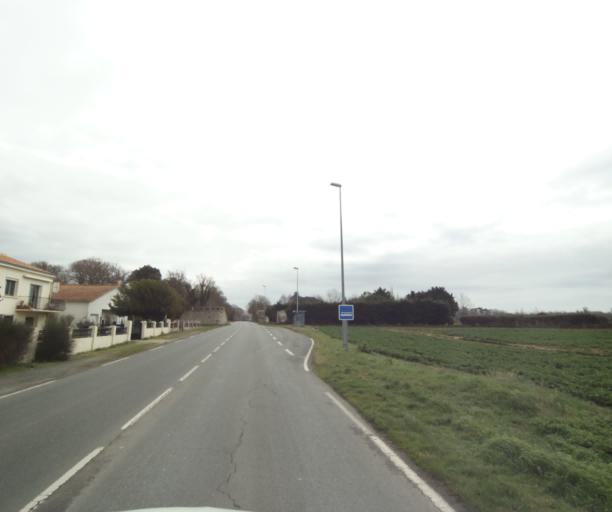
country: FR
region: Poitou-Charentes
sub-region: Departement de la Charente-Maritime
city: Nieul-sur-Mer
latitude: 46.1861
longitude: -1.1789
